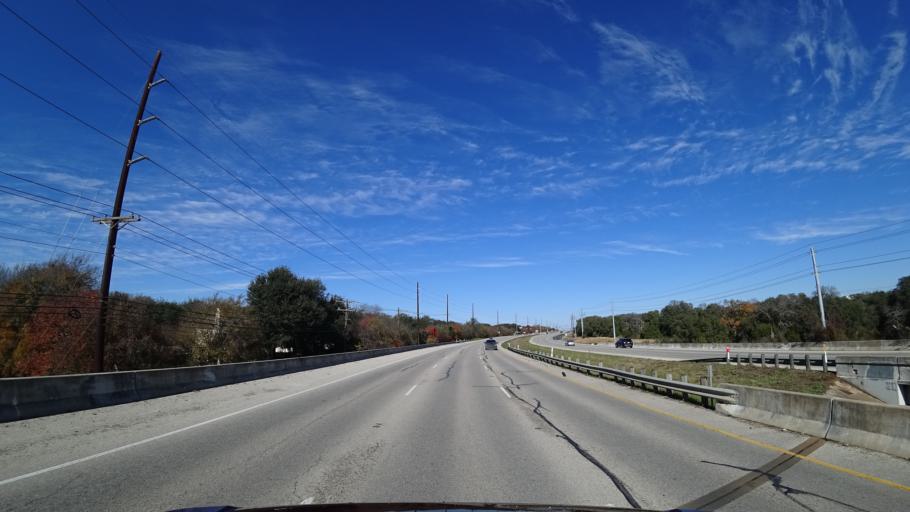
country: US
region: Texas
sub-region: Williamson County
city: Jollyville
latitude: 30.4531
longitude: -97.7514
